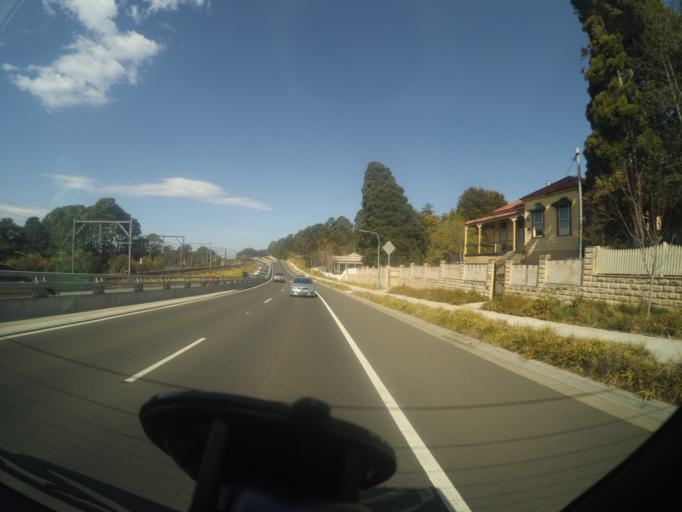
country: AU
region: New South Wales
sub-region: Blue Mountains Municipality
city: Leura
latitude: -33.7123
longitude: 150.3774
